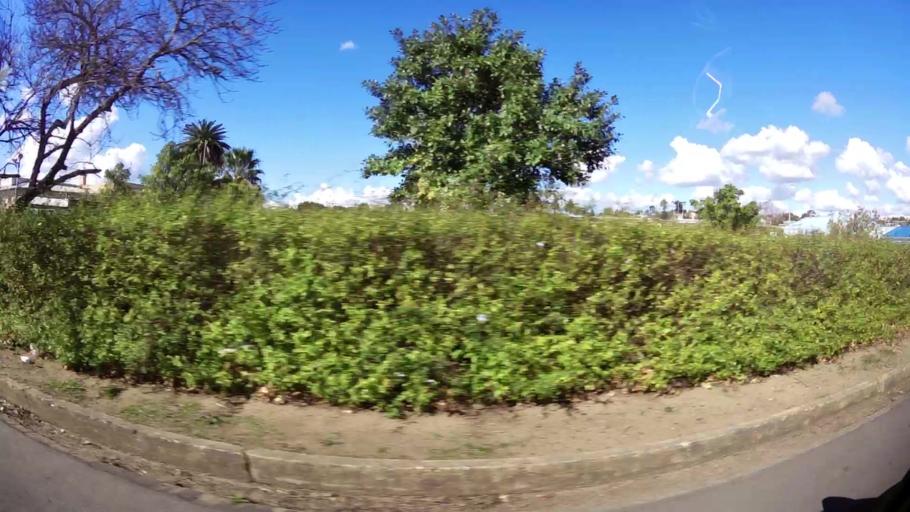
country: ZA
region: Western Cape
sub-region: Overberg District Municipality
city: Swellendam
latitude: -34.0272
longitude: 20.4440
